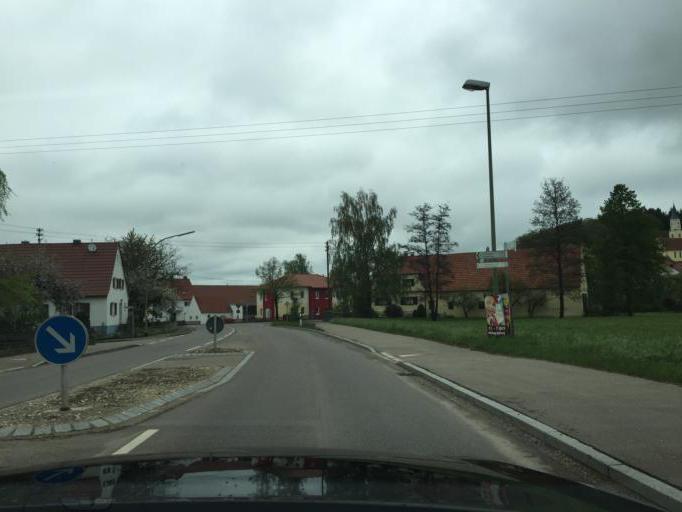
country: DE
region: Bavaria
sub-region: Swabia
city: Buttenwiesen
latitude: 48.5792
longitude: 10.7144
